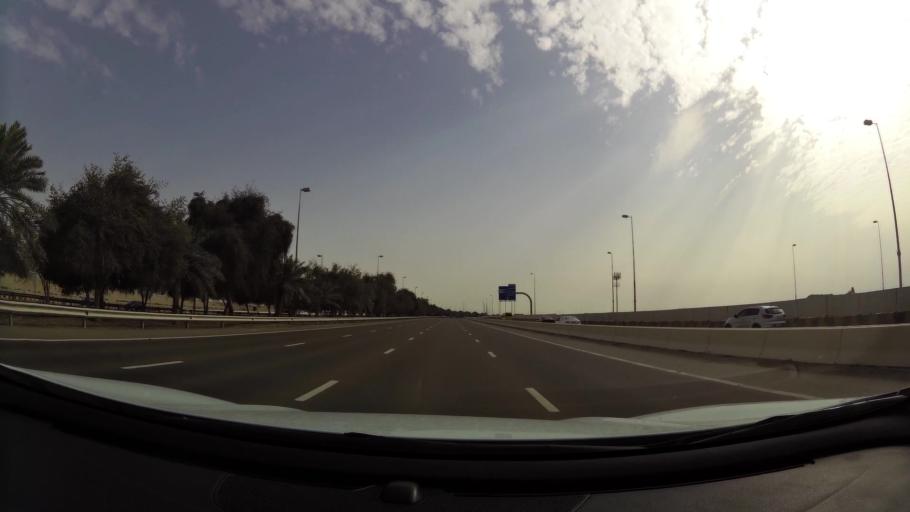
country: AE
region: Abu Dhabi
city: Abu Dhabi
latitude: 24.4247
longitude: 54.6774
